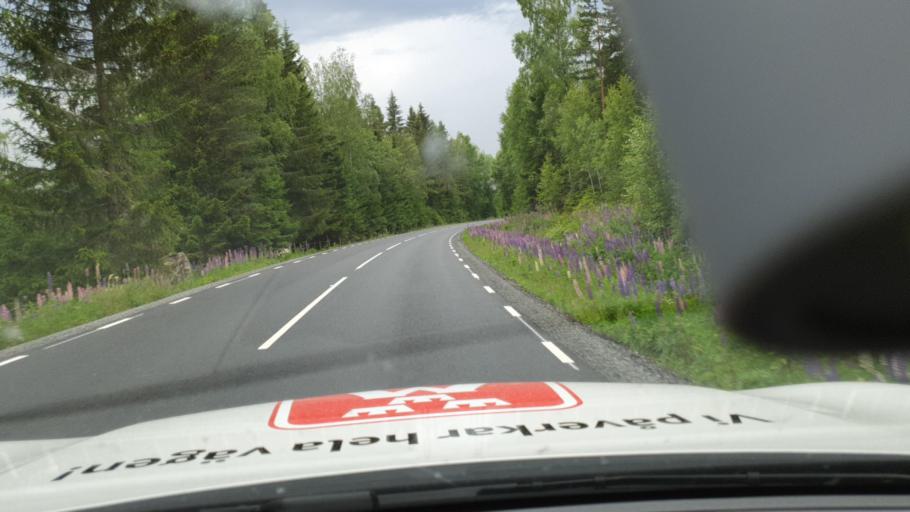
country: SE
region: OErebro
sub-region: Laxa Kommun
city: Laxa
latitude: 58.9014
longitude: 14.4710
